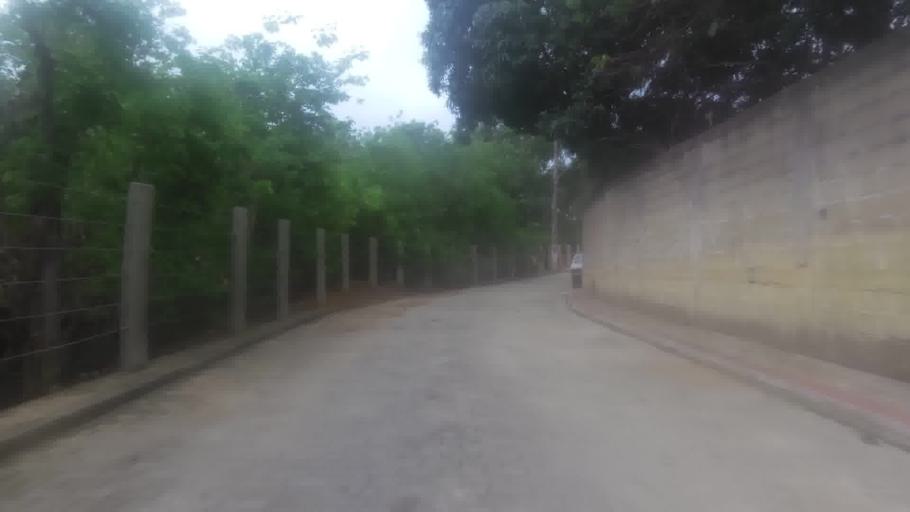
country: BR
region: Espirito Santo
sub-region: Piuma
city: Piuma
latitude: -20.7945
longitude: -40.6054
